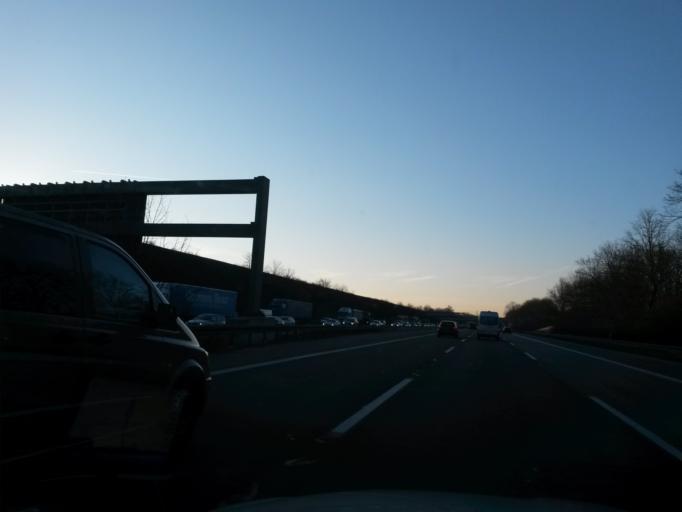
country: DE
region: Bavaria
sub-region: Upper Bavaria
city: Kirchheim bei Muenchen
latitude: 48.1605
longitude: 11.7466
